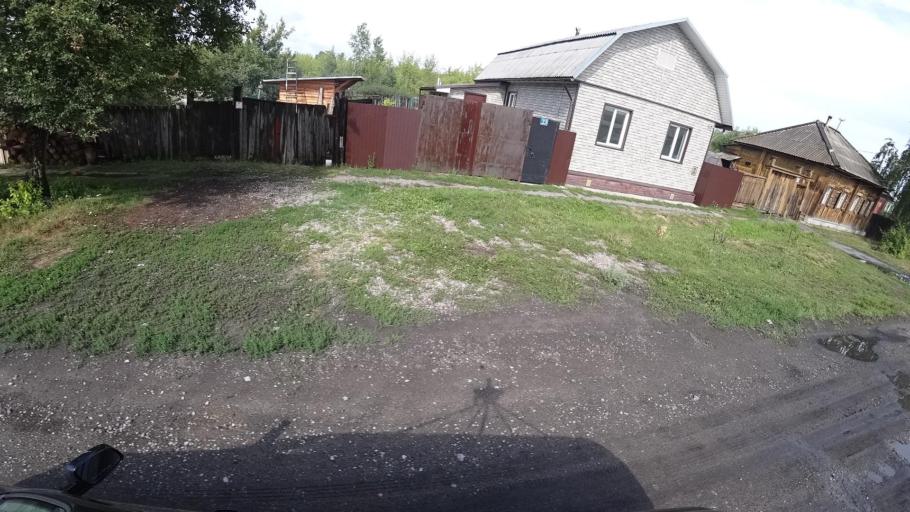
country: RU
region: Sverdlovsk
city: Kamyshlov
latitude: 56.8414
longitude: 62.7289
